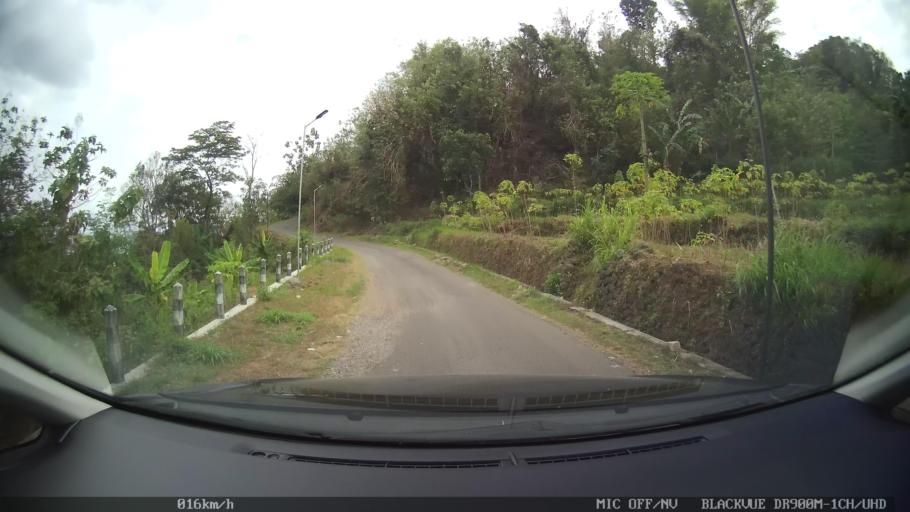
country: ID
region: Central Java
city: Candi Prambanan
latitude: -7.8009
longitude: 110.5211
